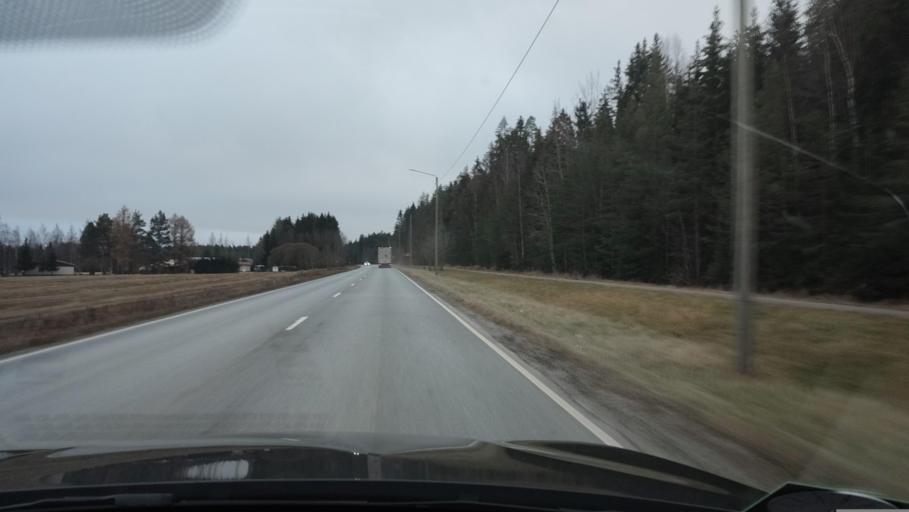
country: FI
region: Southern Ostrobothnia
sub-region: Suupohja
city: Kauhajoki
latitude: 62.4059
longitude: 22.1631
